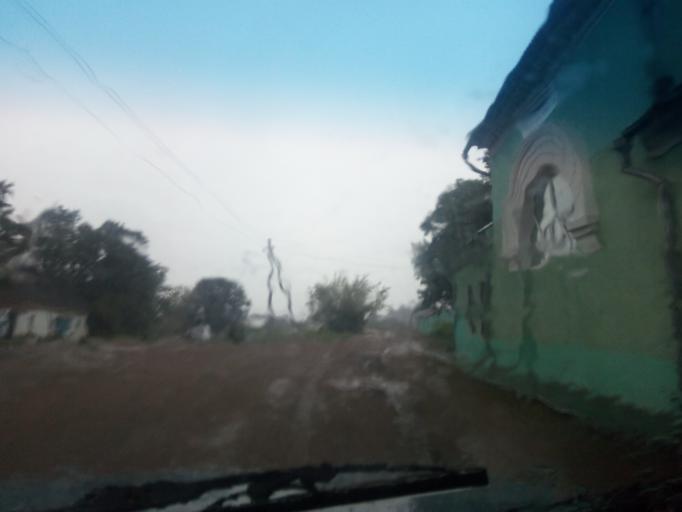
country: BY
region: Vitebsk
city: Dzisna
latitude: 55.6700
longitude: 28.3259
